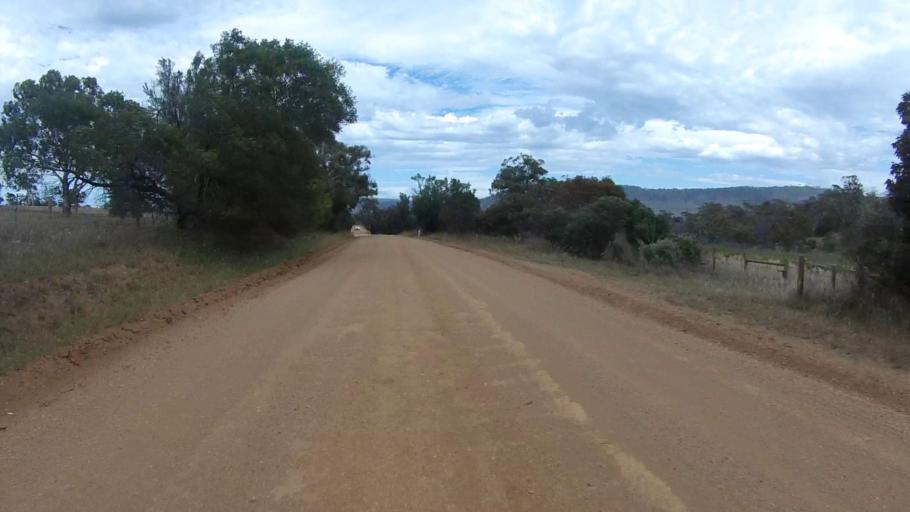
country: AU
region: Tasmania
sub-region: Sorell
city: Sorell
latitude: -42.6983
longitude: 147.4614
